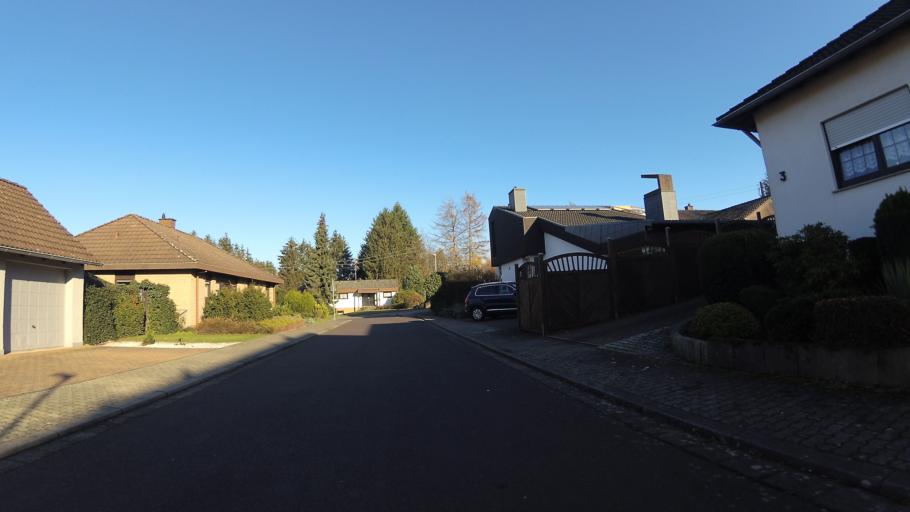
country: DE
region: Saarland
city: Schwalbach
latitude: 49.2957
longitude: 6.8144
